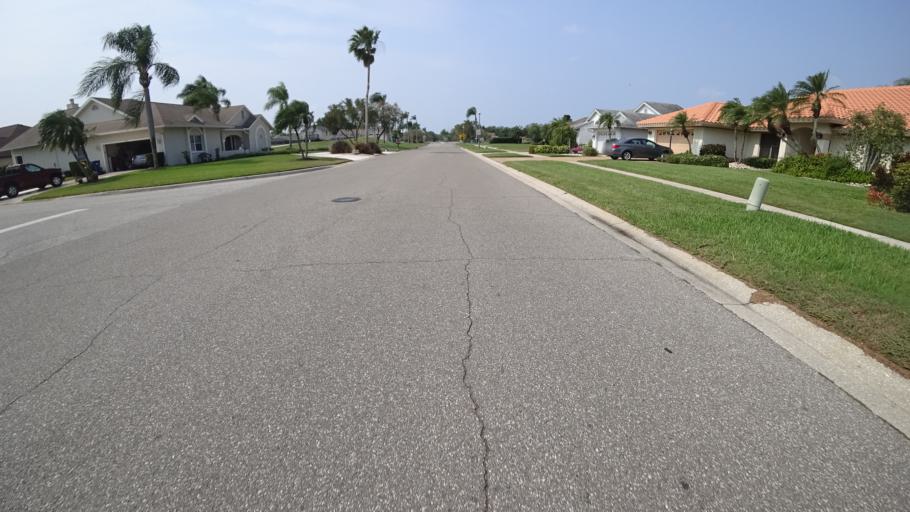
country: US
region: Florida
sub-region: Manatee County
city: Samoset
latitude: 27.4525
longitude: -82.5105
